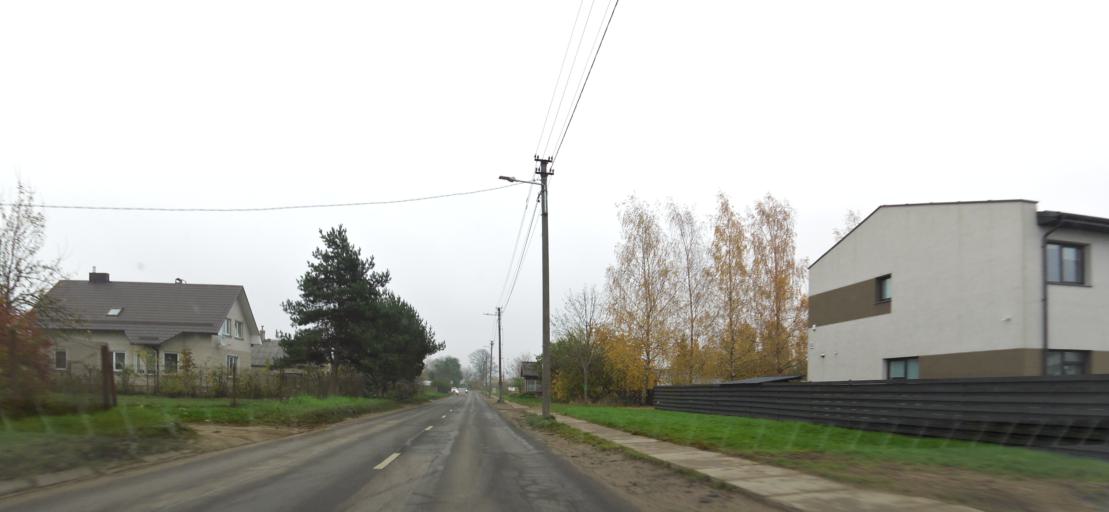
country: LT
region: Vilnius County
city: Rasos
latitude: 54.6608
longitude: 25.3528
